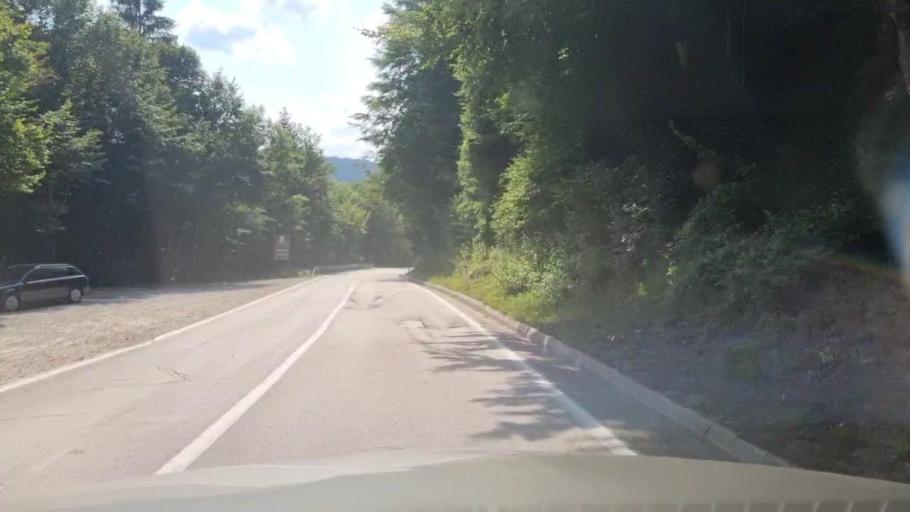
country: BA
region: Federation of Bosnia and Herzegovina
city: Olovo
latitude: 44.1617
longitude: 18.6467
